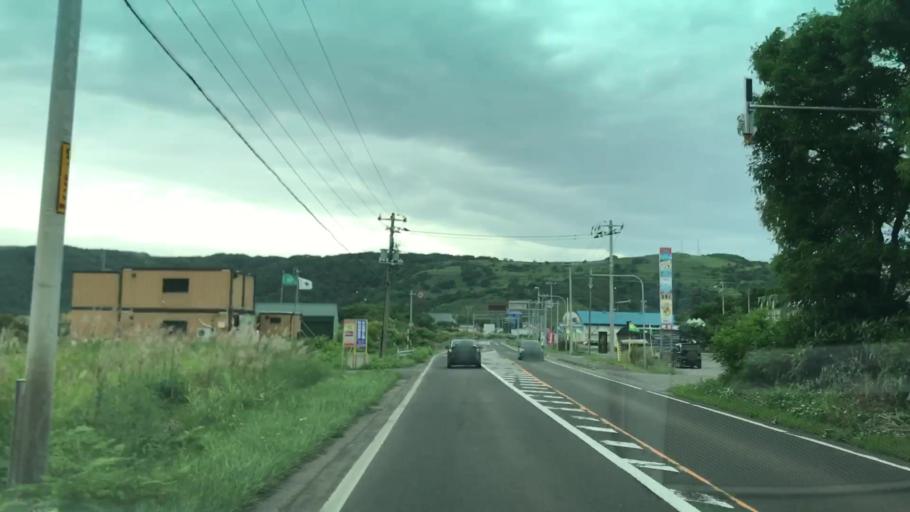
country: JP
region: Hokkaido
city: Iwanai
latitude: 42.8812
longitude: 140.3716
